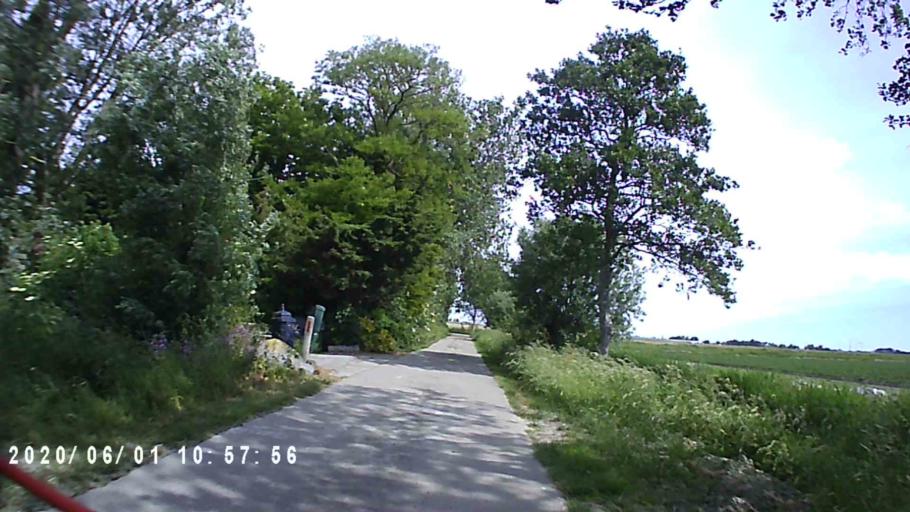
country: NL
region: Friesland
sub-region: Gemeente Franekeradeel
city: Sexbierum
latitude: 53.2003
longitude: 5.4926
